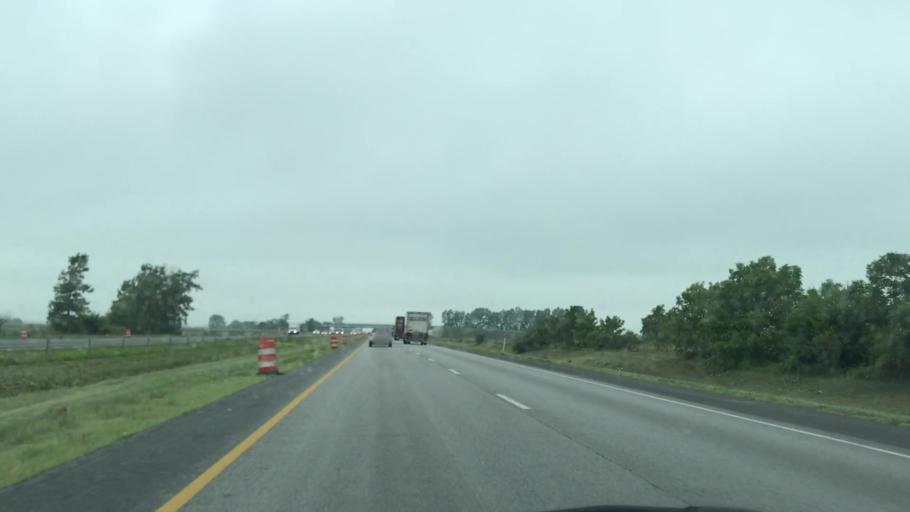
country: US
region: Indiana
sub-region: Boone County
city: Thorntown
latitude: 40.2093
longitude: -86.5894
